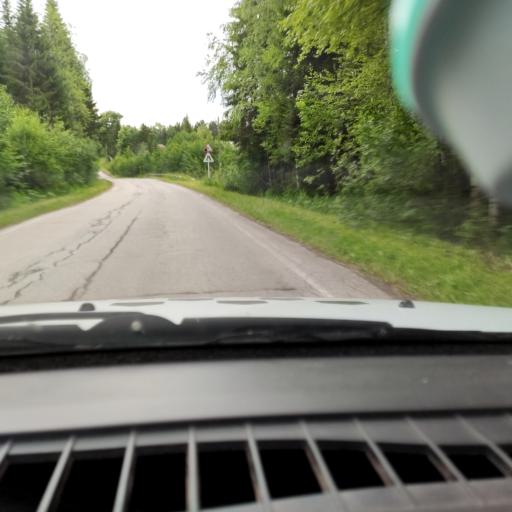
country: RU
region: Perm
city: Lys'va
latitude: 58.1158
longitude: 57.6982
